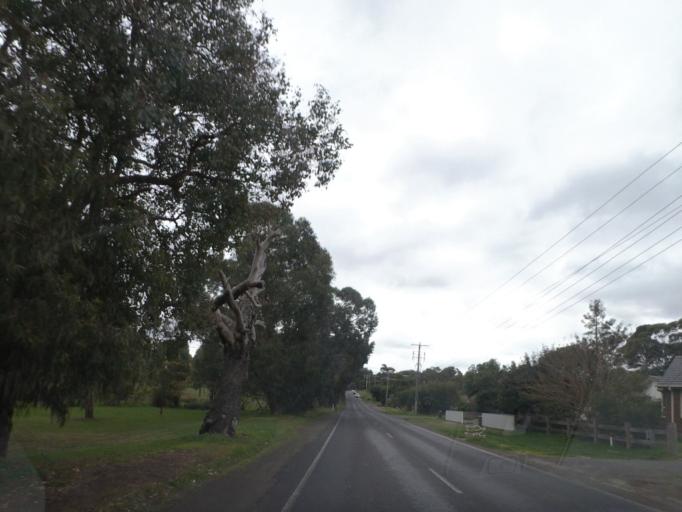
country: AU
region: Victoria
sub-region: Nillumbik
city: Doreen
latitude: -37.6239
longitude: 145.1350
